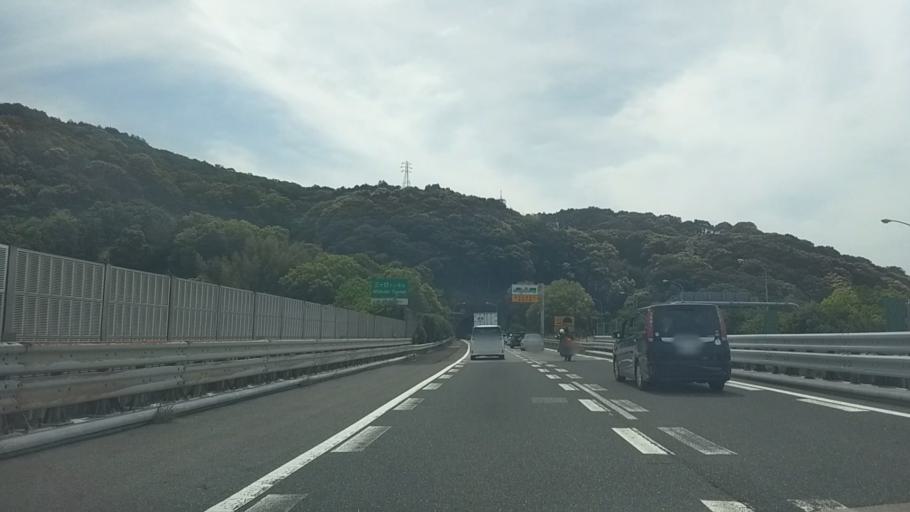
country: JP
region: Shizuoka
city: Kosai-shi
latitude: 34.8147
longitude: 137.5525
